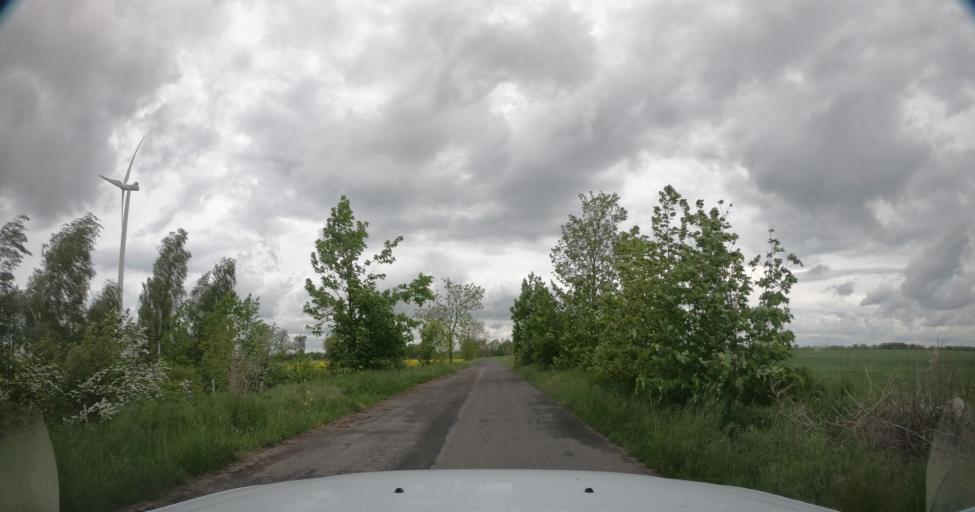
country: PL
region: West Pomeranian Voivodeship
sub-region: Powiat pyrzycki
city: Kozielice
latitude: 53.1156
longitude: 14.8119
